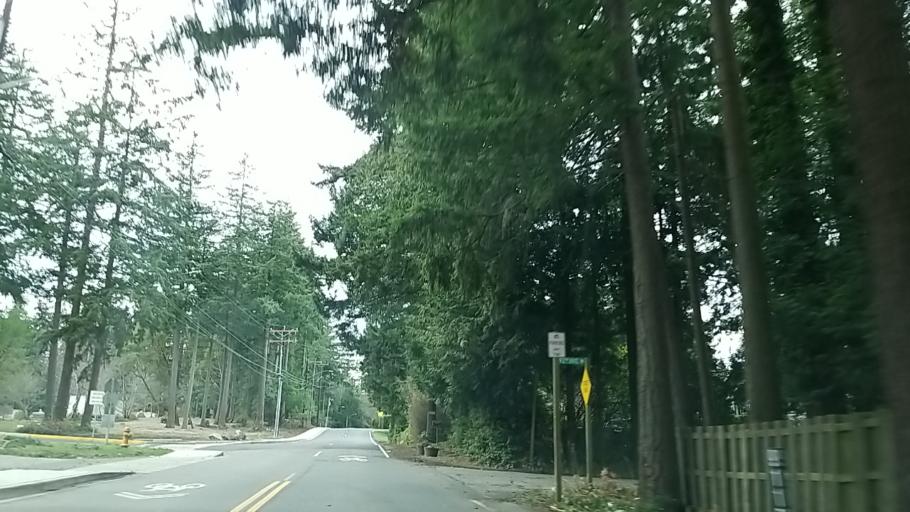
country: US
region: Washington
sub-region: Snohomish County
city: Esperance
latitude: 47.7851
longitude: -122.3554
